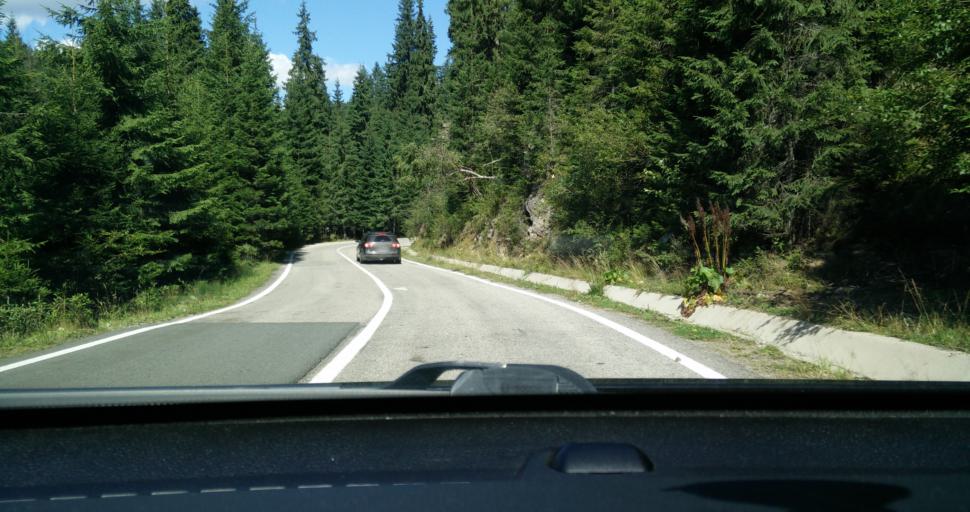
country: RO
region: Alba
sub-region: Comuna Sugag
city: Sugag
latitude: 45.5308
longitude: 23.6443
